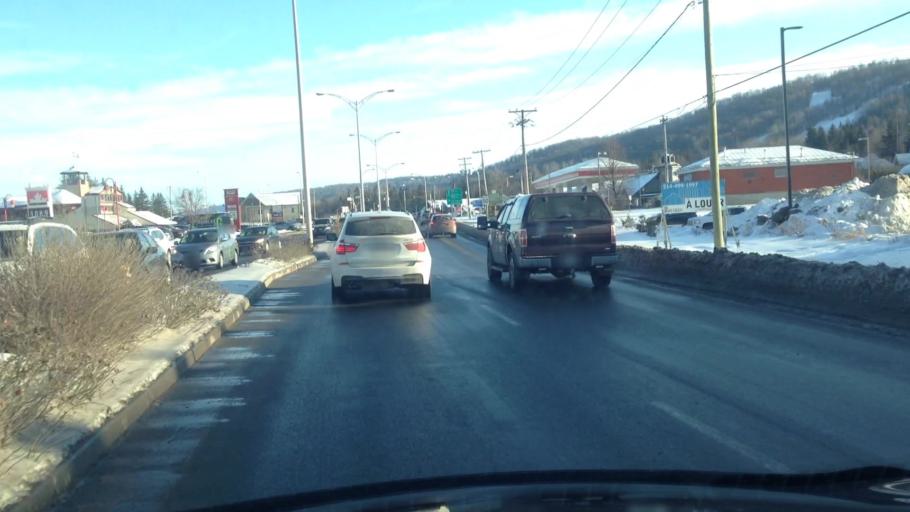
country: CA
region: Quebec
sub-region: Laurentides
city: Saint-Sauveur
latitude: 45.8916
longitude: -74.1506
